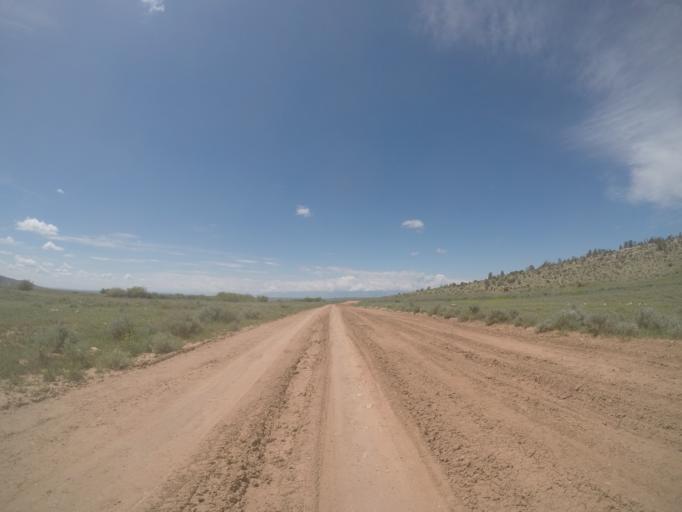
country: US
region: Montana
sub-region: Yellowstone County
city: Laurel
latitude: 45.2408
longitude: -108.6694
